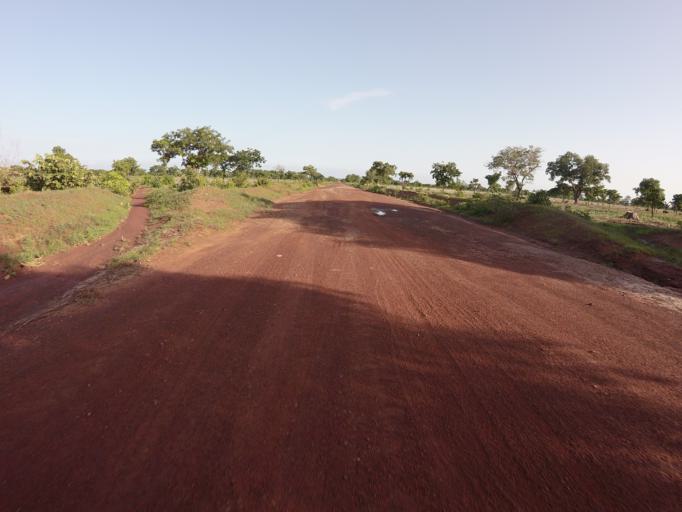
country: TG
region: Savanes
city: Sansanne-Mango
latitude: 10.3765
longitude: -0.0944
